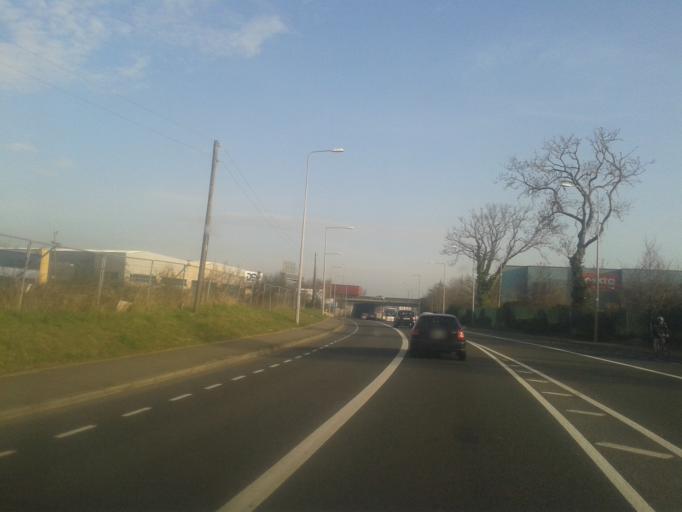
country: IE
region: Leinster
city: Beaumont
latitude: 53.4081
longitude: -6.2378
